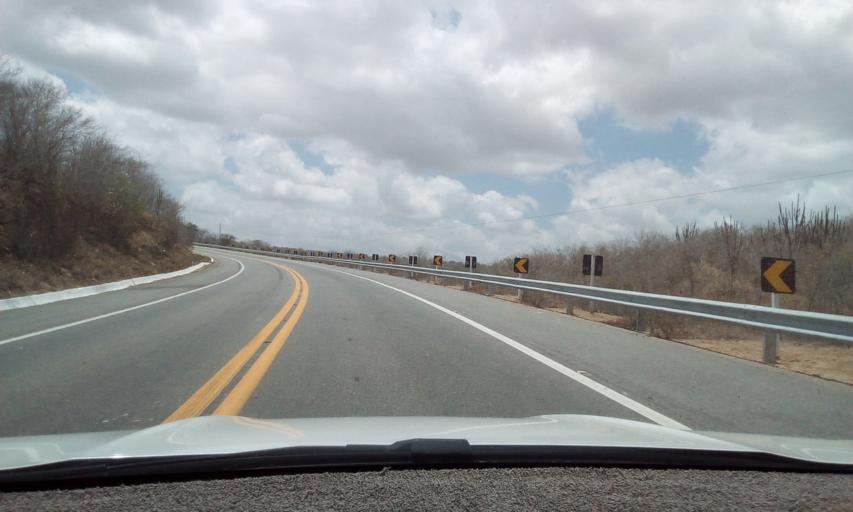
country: BR
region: Paraiba
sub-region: Boqueirao
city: Boqueirao
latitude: -7.6701
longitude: -36.0808
